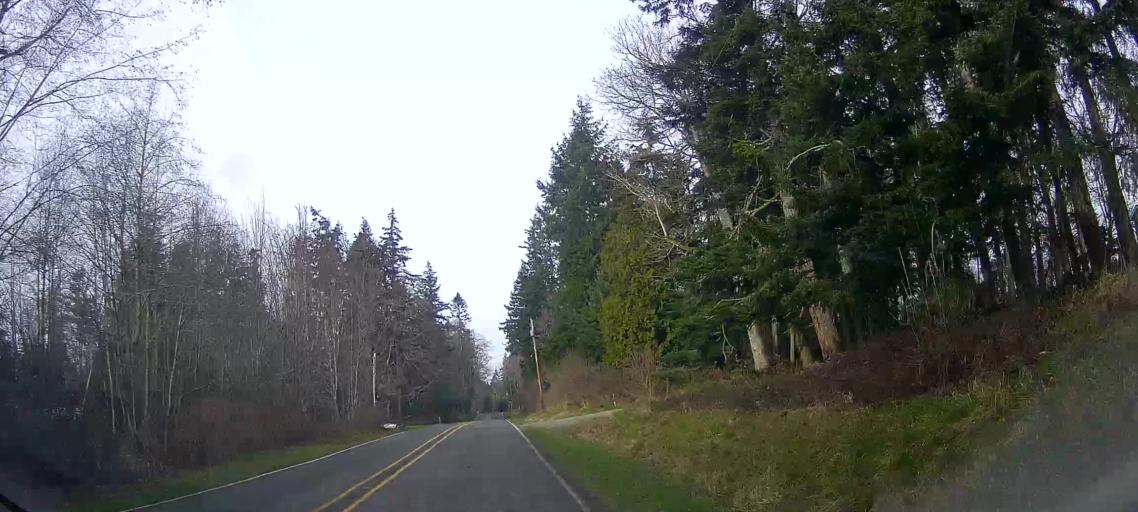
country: US
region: Washington
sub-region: Island County
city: Langley
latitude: 48.0760
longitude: -122.3739
